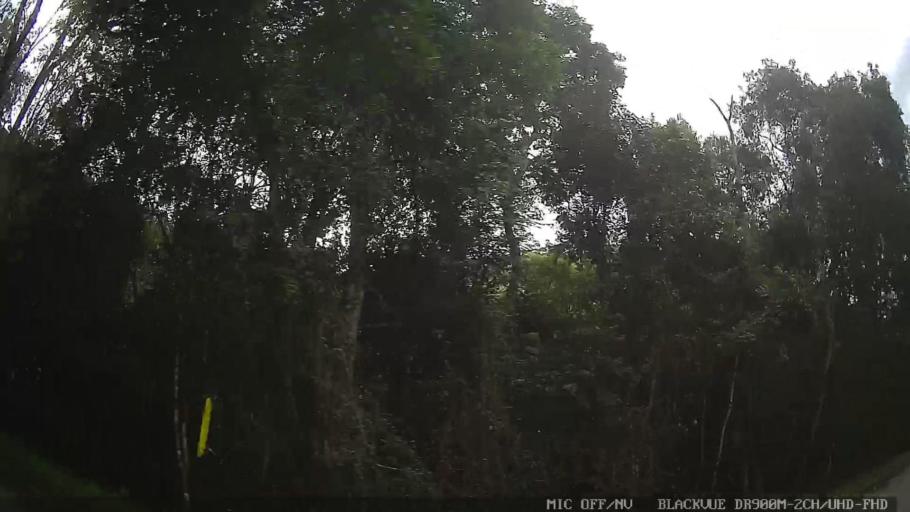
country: BR
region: Sao Paulo
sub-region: Santa Branca
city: Santa Branca
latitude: -23.5404
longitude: -45.6945
